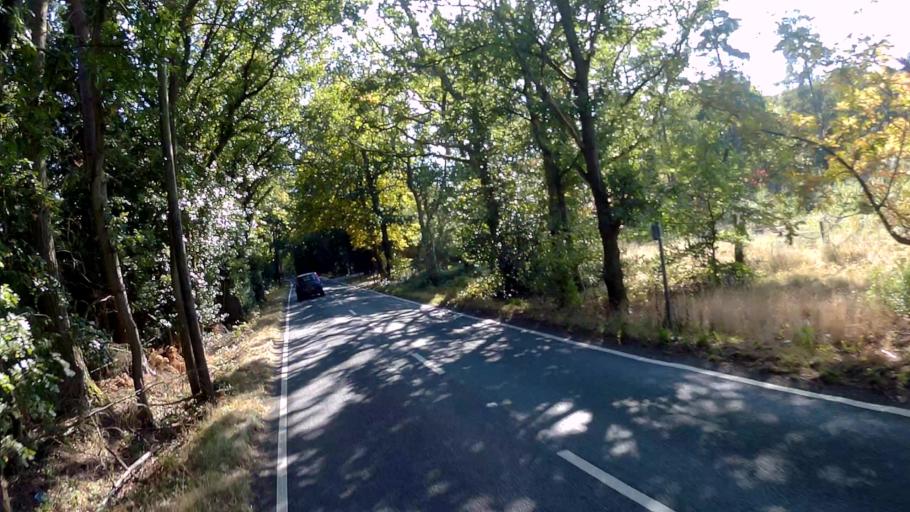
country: GB
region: England
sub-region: Surrey
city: Farnham
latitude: 51.1964
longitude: -0.7724
